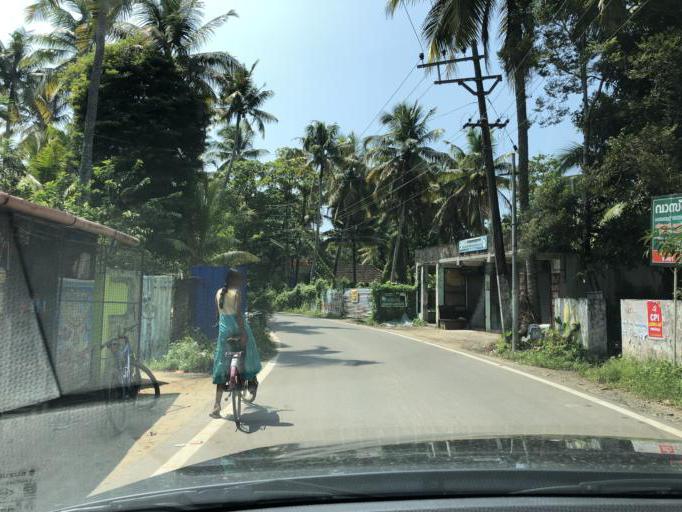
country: IN
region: Kerala
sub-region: Ernakulam
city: Cochin
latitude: 9.9894
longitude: 76.2279
